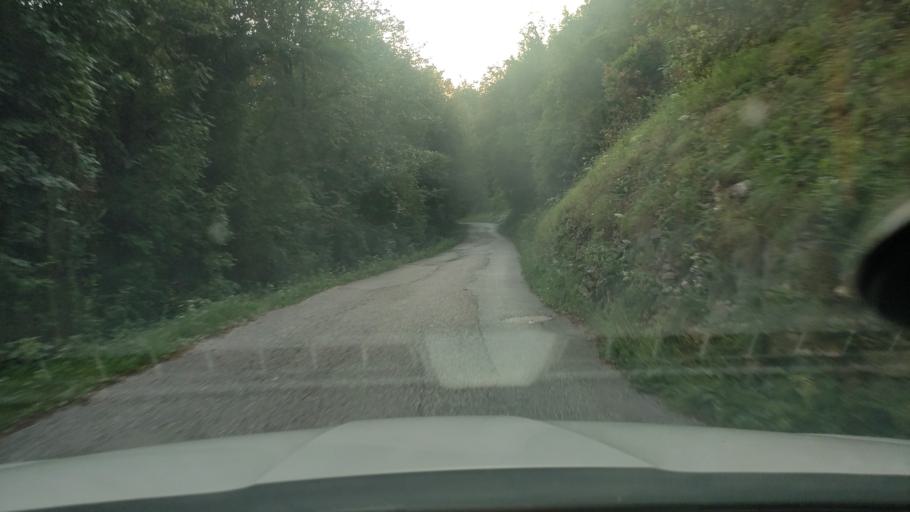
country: IT
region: Friuli Venezia Giulia
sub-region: Provincia di Udine
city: Cras
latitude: 46.2171
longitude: 13.6354
